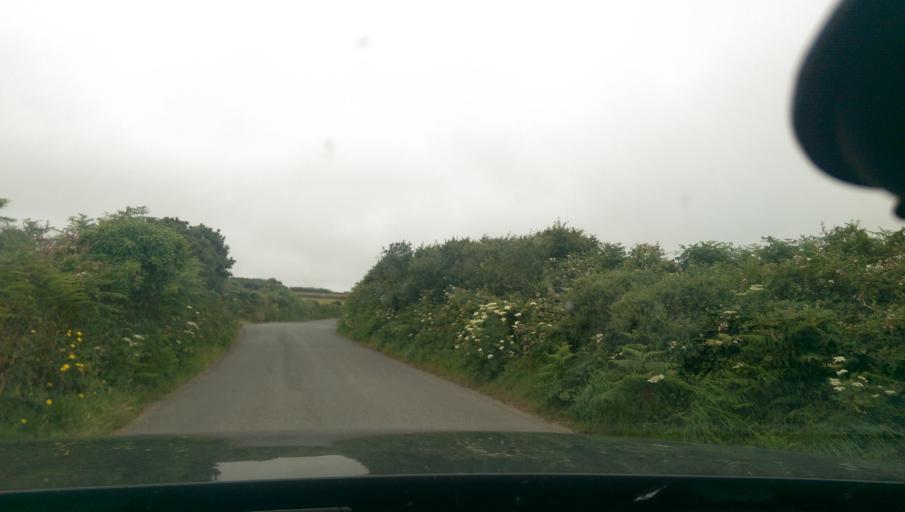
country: GB
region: England
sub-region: Cornwall
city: St. Buryan
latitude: 50.0944
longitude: -5.6468
